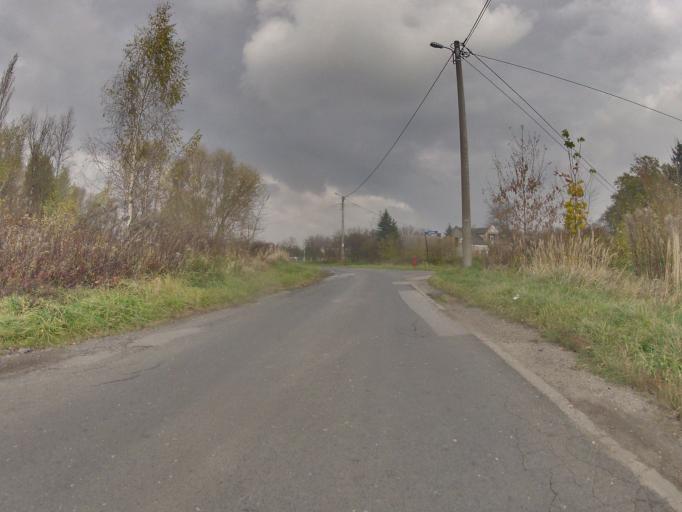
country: PL
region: Lesser Poland Voivodeship
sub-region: Powiat wielicki
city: Wegrzce Wielkie
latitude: 50.0491
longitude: 20.1015
